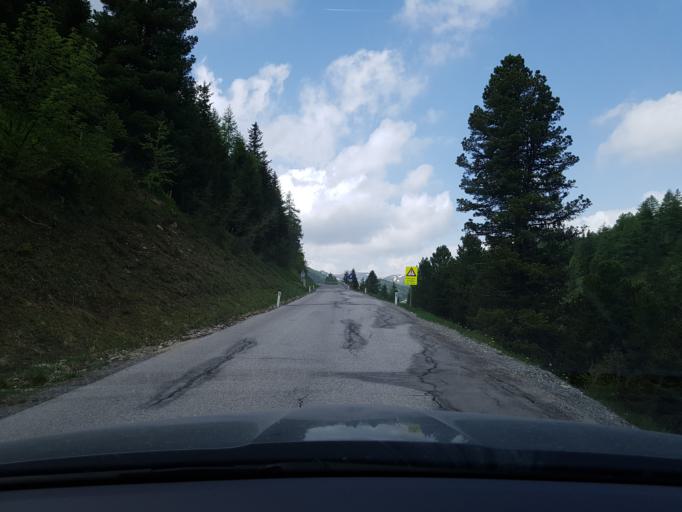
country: AT
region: Salzburg
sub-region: Politischer Bezirk Tamsweg
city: Thomatal
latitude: 46.9772
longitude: 13.7729
